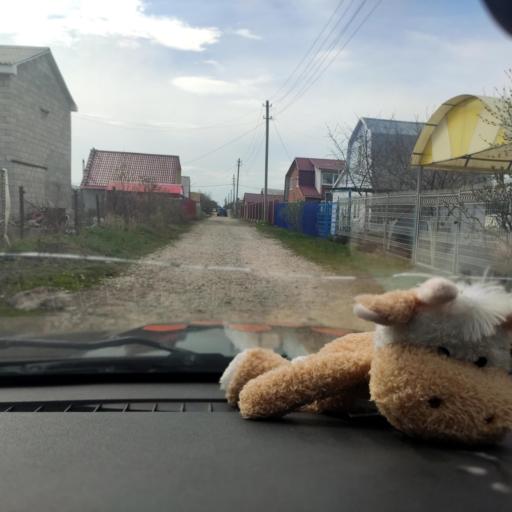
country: RU
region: Samara
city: Podstepki
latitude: 53.5951
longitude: 49.2270
